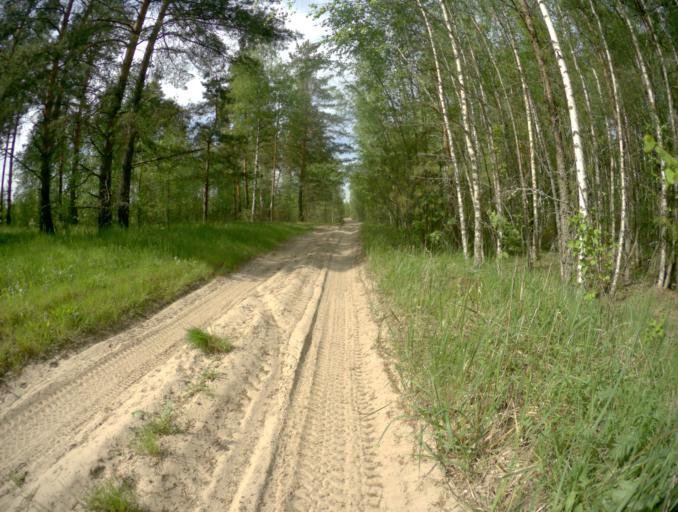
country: RU
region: Vladimir
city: Ivanishchi
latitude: 55.7390
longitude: 40.3640
